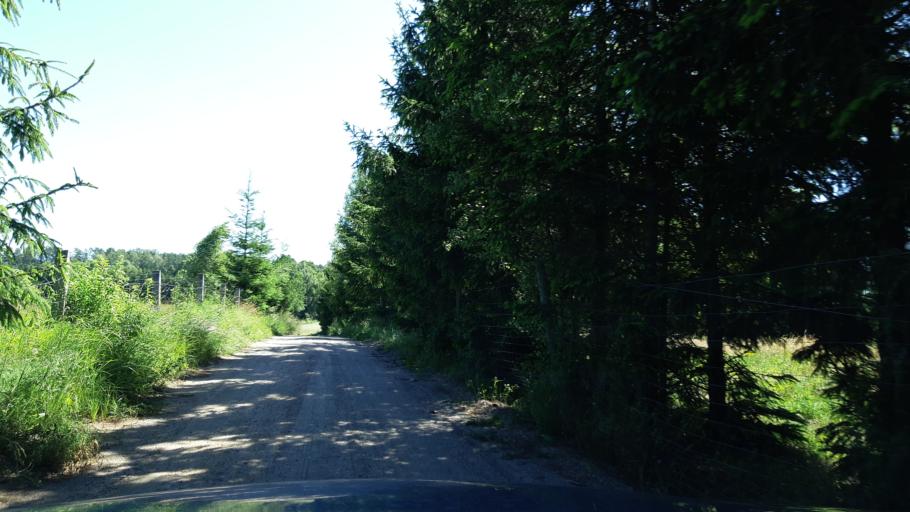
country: PL
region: Warmian-Masurian Voivodeship
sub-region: Powiat piski
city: Ruciane-Nida
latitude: 53.7067
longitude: 21.4799
